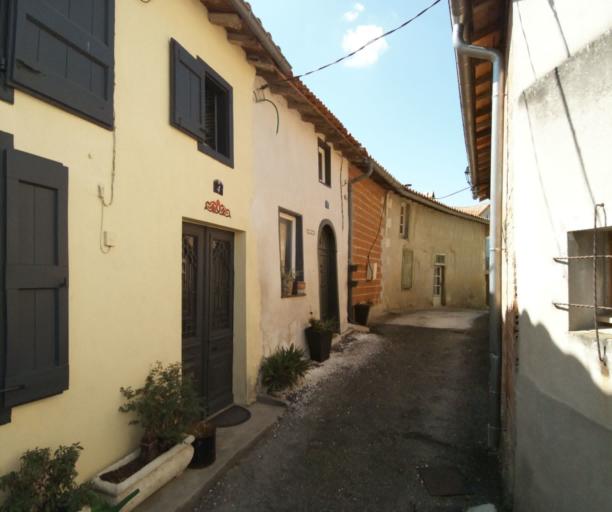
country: FR
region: Midi-Pyrenees
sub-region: Departement de la Haute-Garonne
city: Saint-Felix-Lauragais
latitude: 43.4895
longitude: 1.8973
